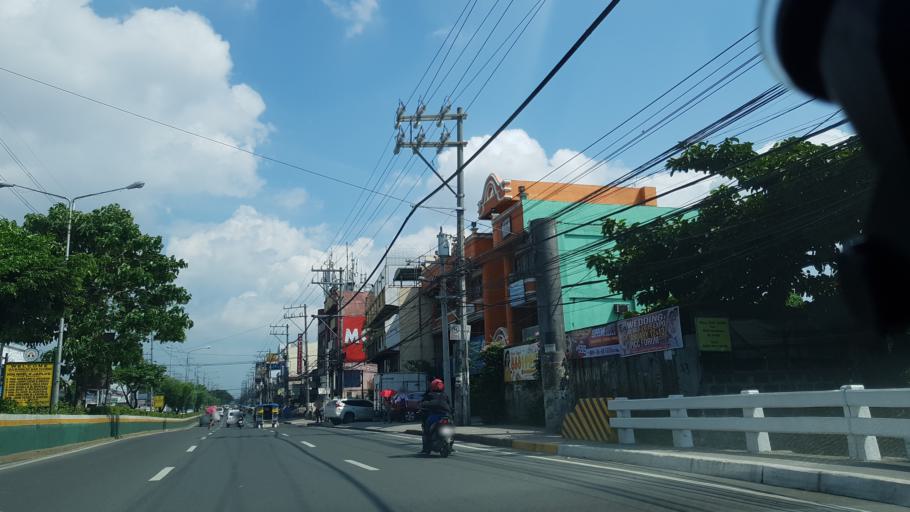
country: PH
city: Sambayanihan People's Village
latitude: 14.4743
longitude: 121.0023
